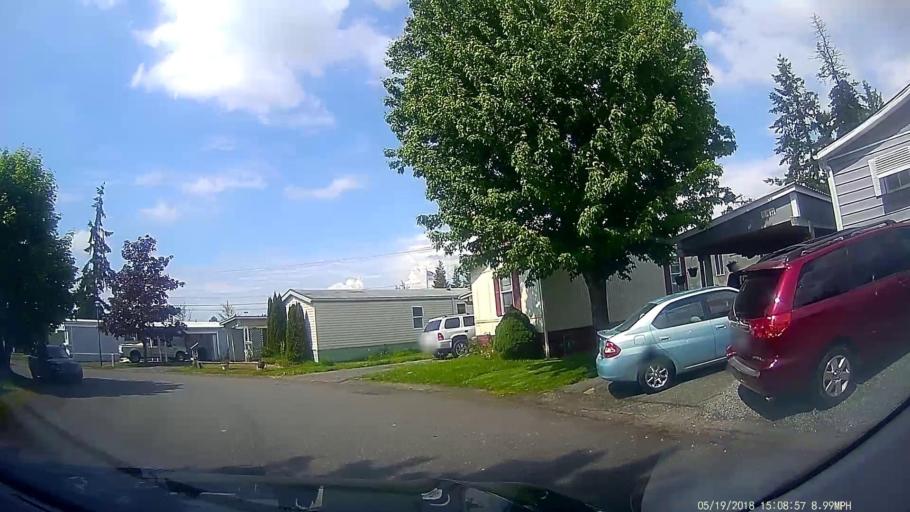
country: US
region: Washington
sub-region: Skagit County
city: Mount Vernon
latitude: 48.4204
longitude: -122.3070
